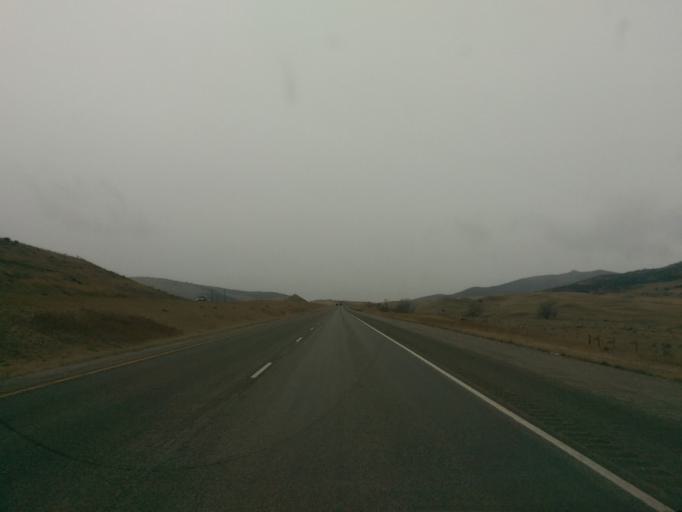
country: US
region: Montana
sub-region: Gallatin County
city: Three Forks
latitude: 45.9054
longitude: -111.8025
